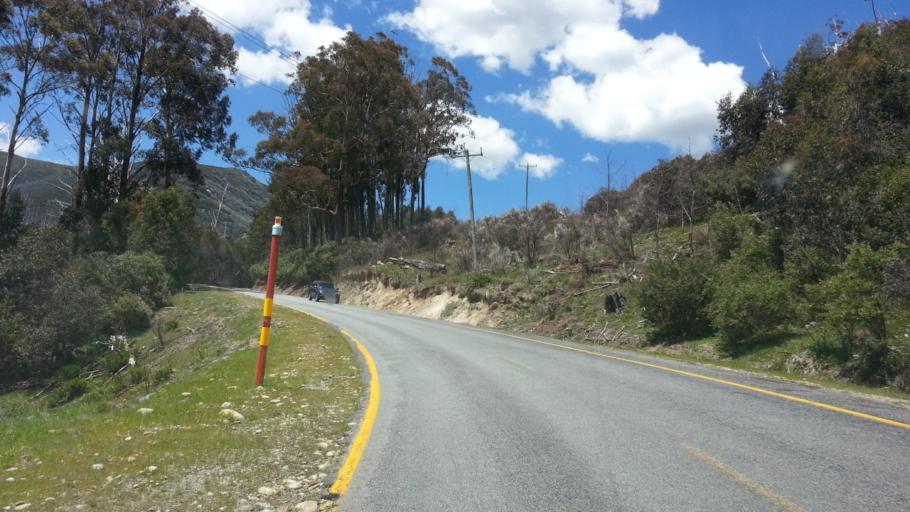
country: AU
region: Victoria
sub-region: Alpine
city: Mount Beauty
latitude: -36.8451
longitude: 147.2627
